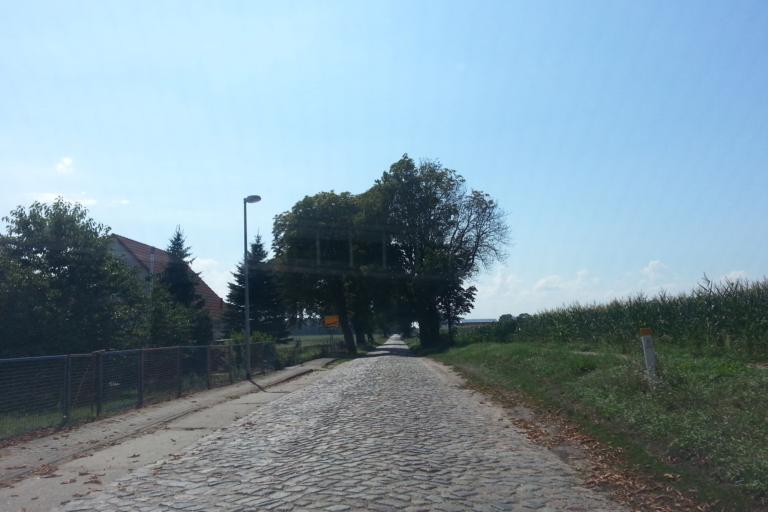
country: DE
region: Mecklenburg-Vorpommern
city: Ferdinandshof
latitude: 53.7003
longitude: 13.8283
